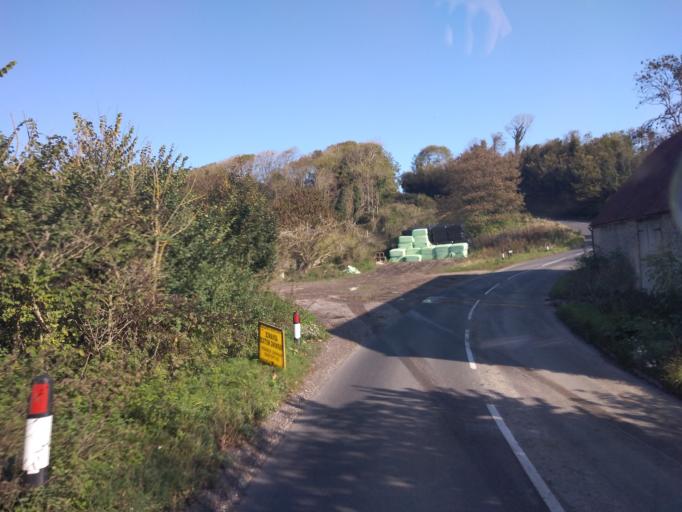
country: GB
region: England
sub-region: East Sussex
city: Seaford
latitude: 50.7944
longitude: 0.1493
